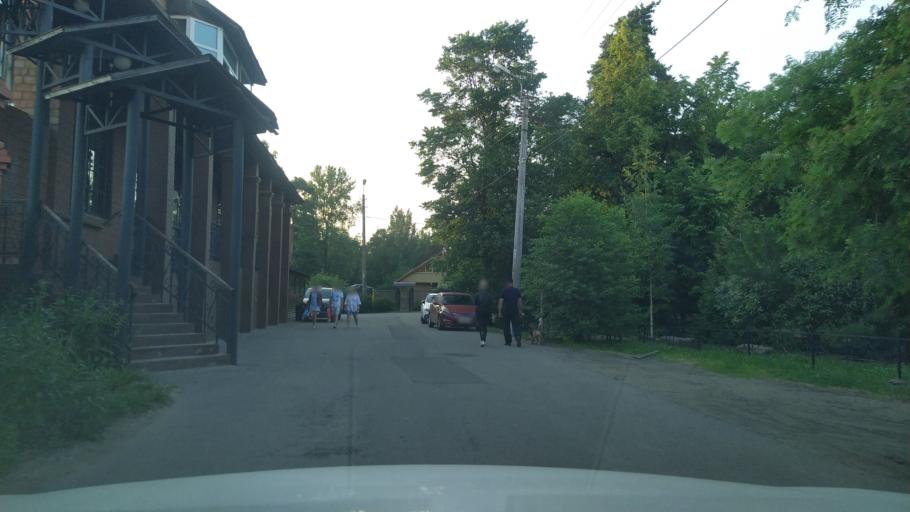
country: RU
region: St.-Petersburg
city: Sestroretsk
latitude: 60.0924
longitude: 29.9482
